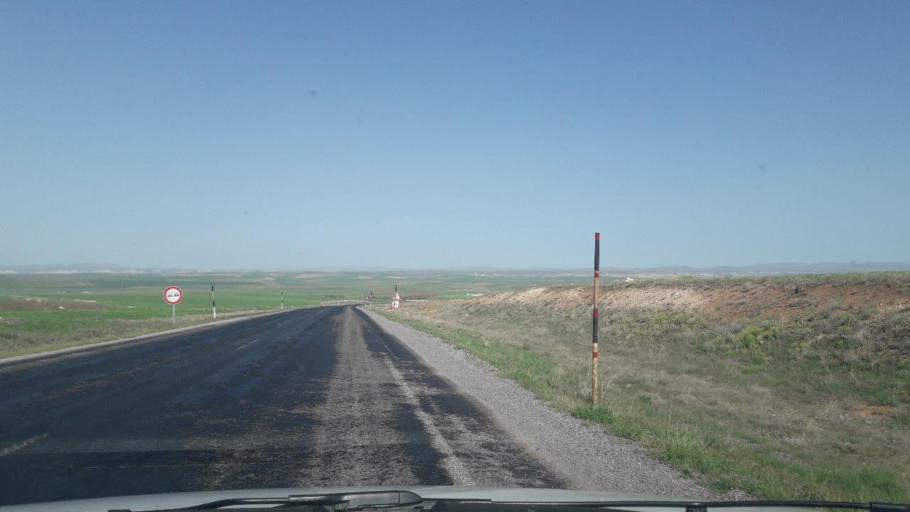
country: TR
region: Sivas
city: Kangal
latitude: 39.1719
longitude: 37.4611
